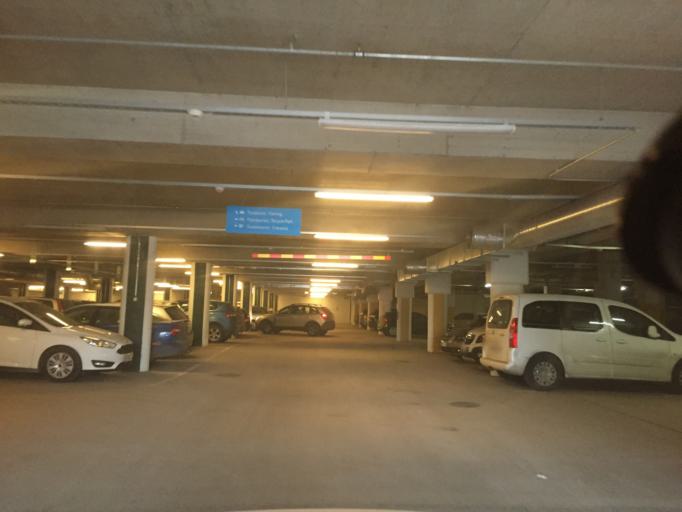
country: FI
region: Uusimaa
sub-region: Helsinki
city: Otaniemi
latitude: 60.1710
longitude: 24.8009
